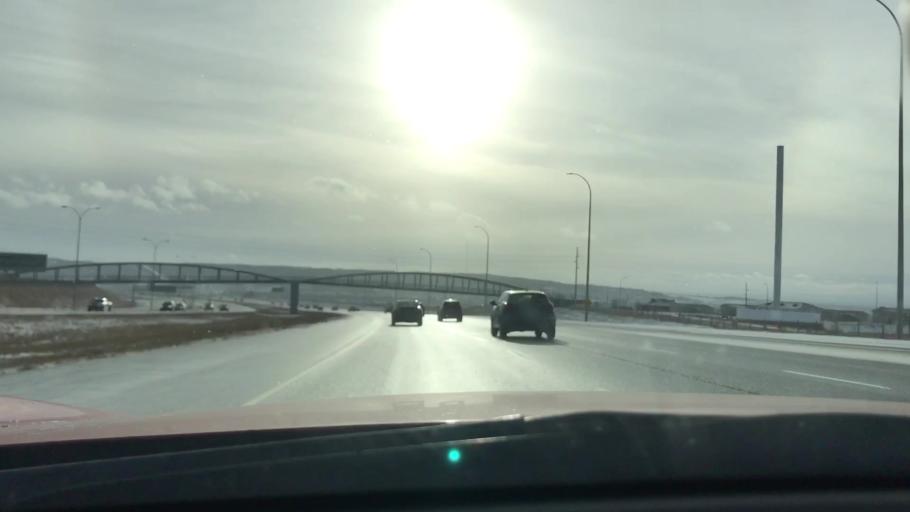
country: CA
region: Alberta
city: Calgary
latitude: 51.1270
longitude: -114.2310
